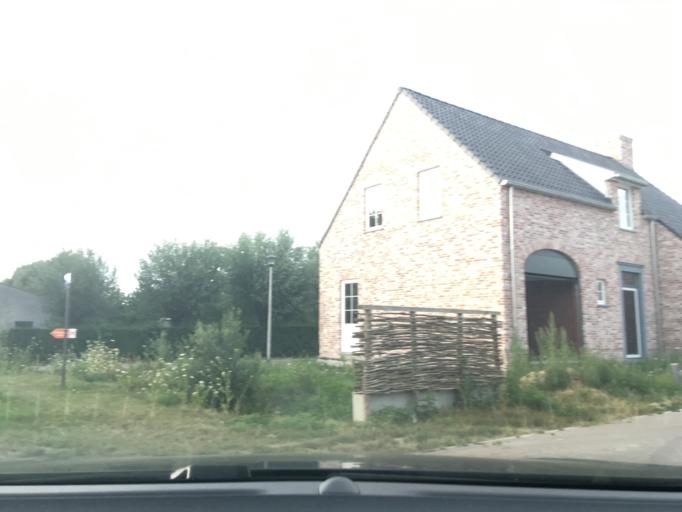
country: BE
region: Flanders
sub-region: Provincie West-Vlaanderen
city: Izegem
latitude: 50.9130
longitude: 3.1905
